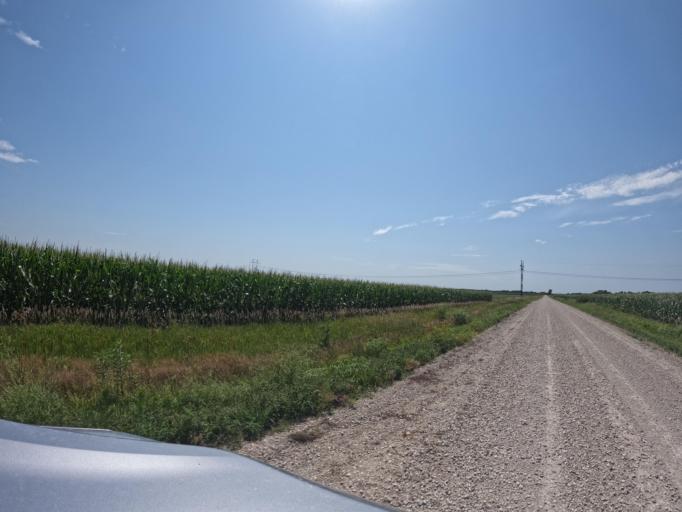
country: US
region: Iowa
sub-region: Henry County
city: Mount Pleasant
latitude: 40.9011
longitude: -91.6366
